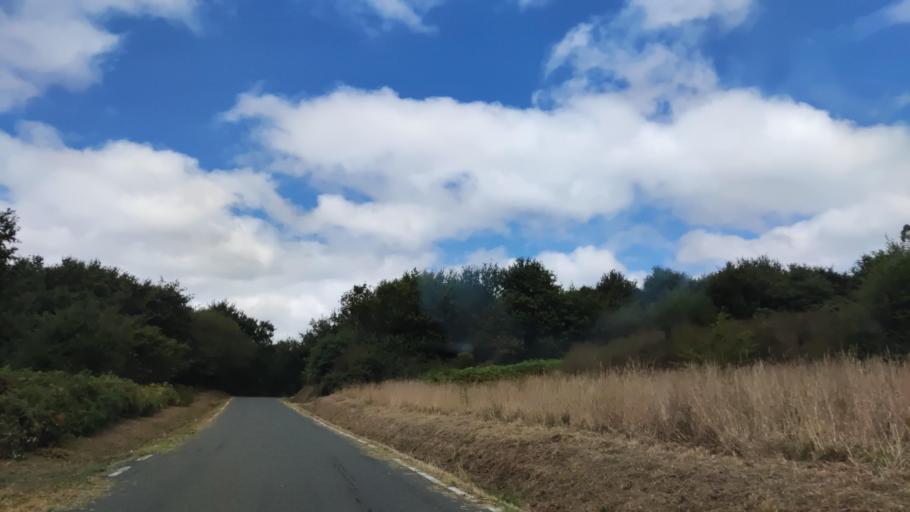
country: ES
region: Galicia
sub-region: Provincia da Coruna
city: Rois
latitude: 42.7464
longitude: -8.6981
